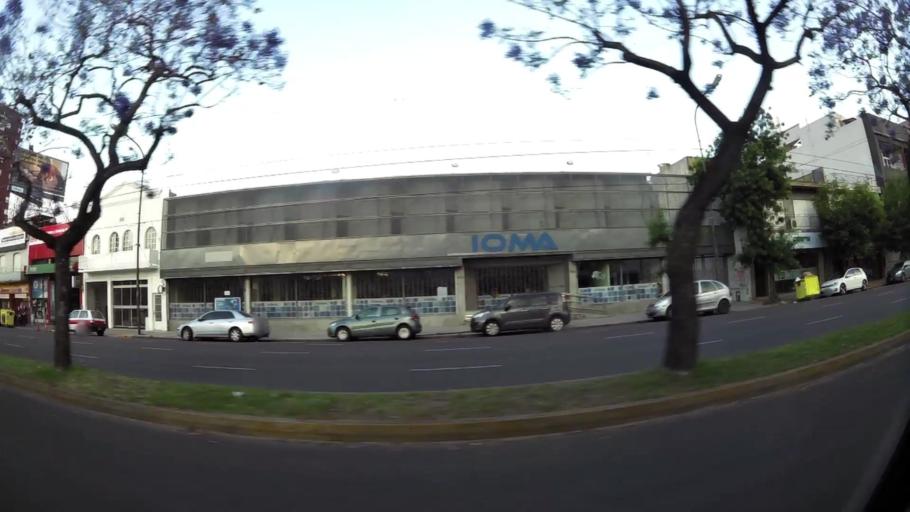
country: AR
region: Buenos Aires
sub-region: Partido de San Isidro
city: San Isidro
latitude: -34.4863
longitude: -58.5023
